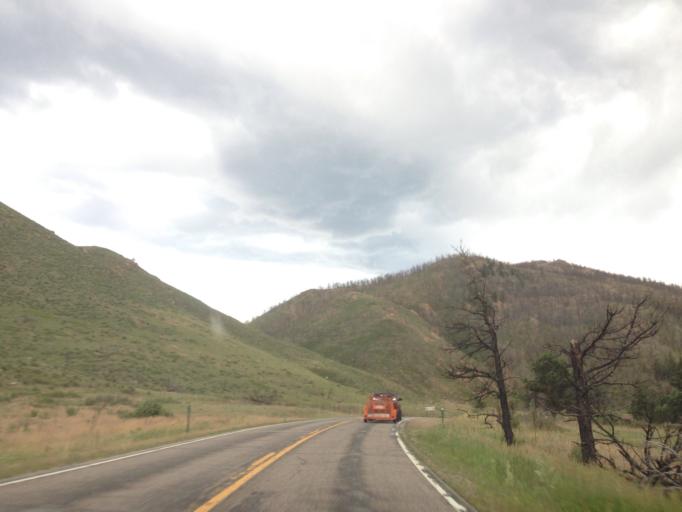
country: US
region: Colorado
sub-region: Larimer County
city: Laporte
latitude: 40.6939
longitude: -105.4337
